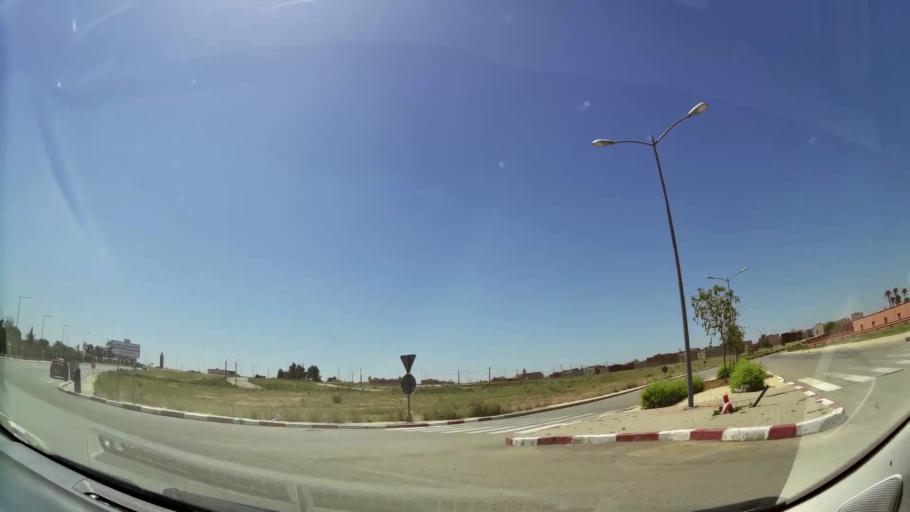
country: MA
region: Oriental
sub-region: Oujda-Angad
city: Oujda
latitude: 34.6673
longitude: -1.8632
